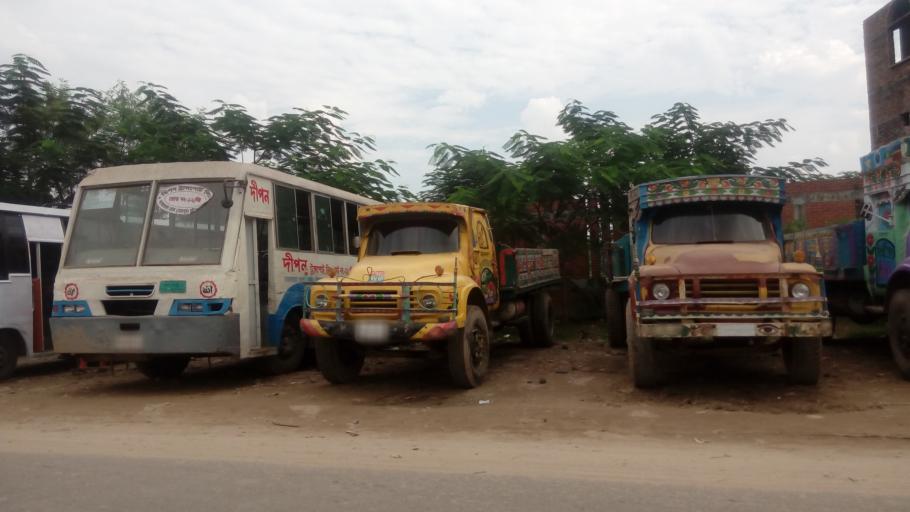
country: BD
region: Dhaka
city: Azimpur
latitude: 23.7529
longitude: 90.3546
